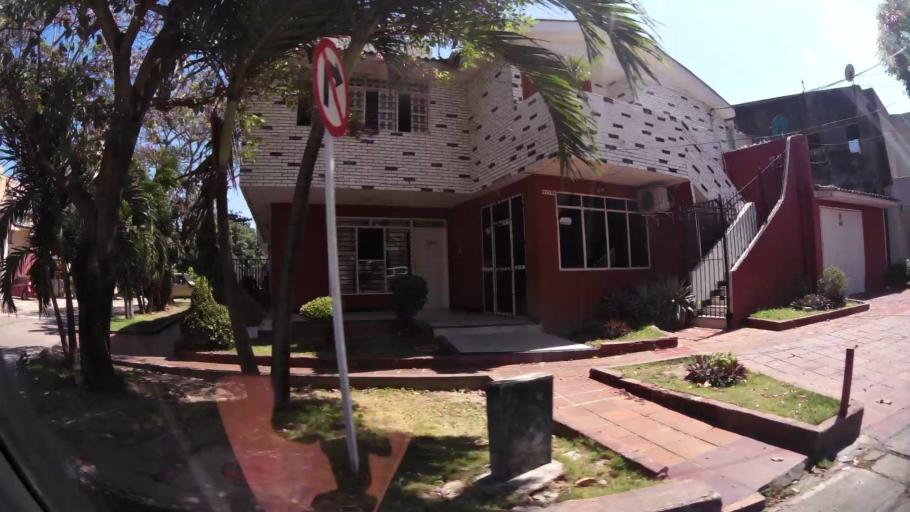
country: CO
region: Atlantico
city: Barranquilla
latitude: 10.9920
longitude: -74.8098
